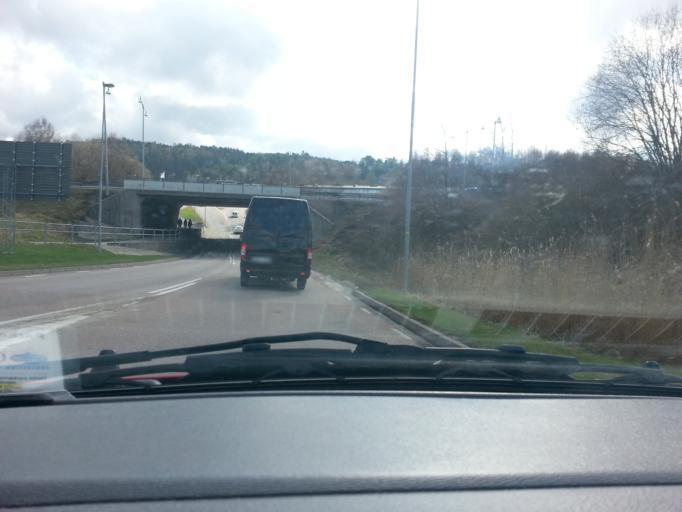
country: SE
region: Vaestra Goetaland
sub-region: Partille Kommun
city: Partille
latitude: 57.7405
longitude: 12.1259
